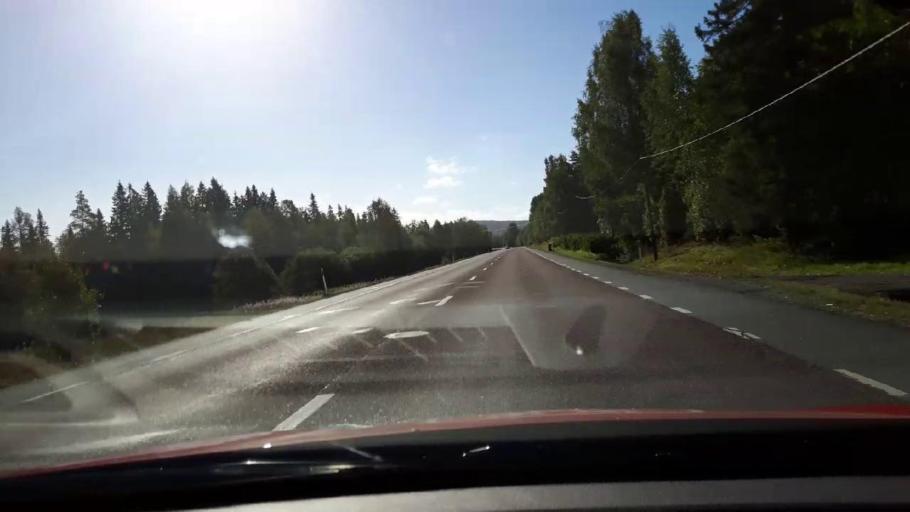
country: SE
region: Jaemtland
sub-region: Braecke Kommun
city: Braecke
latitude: 62.9230
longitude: 15.2308
